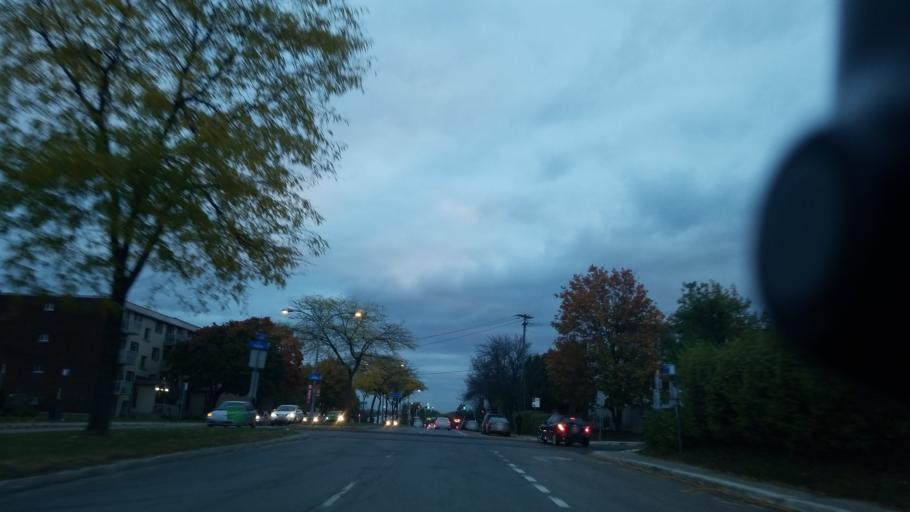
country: CA
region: Quebec
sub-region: Laval
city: Laval
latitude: 45.5616
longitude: -73.7149
